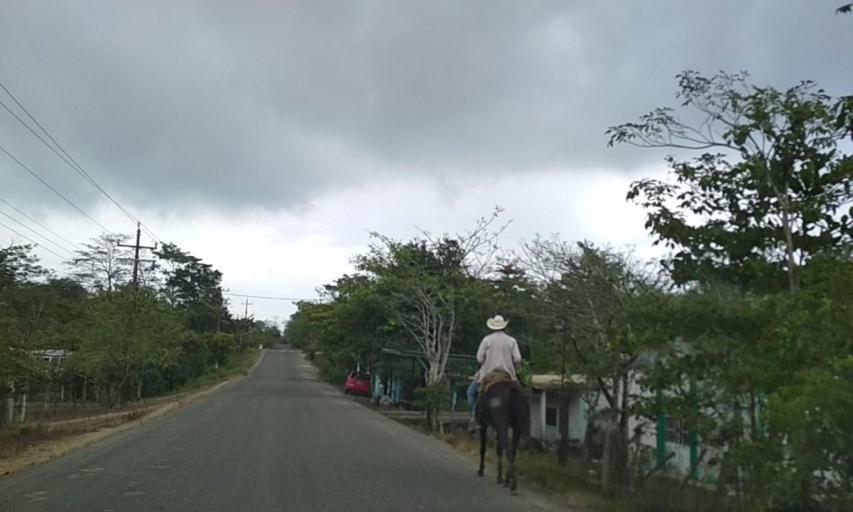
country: MX
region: Tabasco
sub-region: Huimanguillo
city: Francisco Rueda
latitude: 17.5699
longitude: -94.1103
